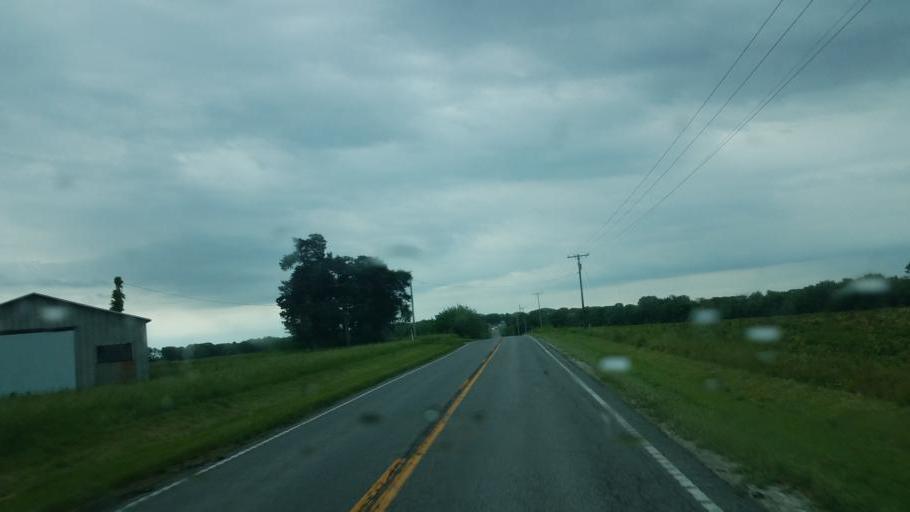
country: US
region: Missouri
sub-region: Moniteau County
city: California
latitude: 38.8228
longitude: -92.6033
